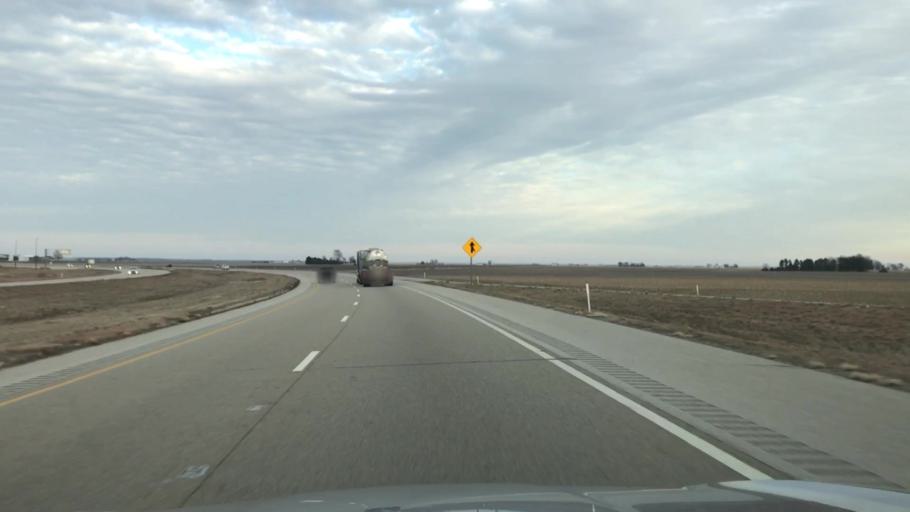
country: US
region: Illinois
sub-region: Logan County
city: Lincoln
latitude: 40.1853
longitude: -89.3149
